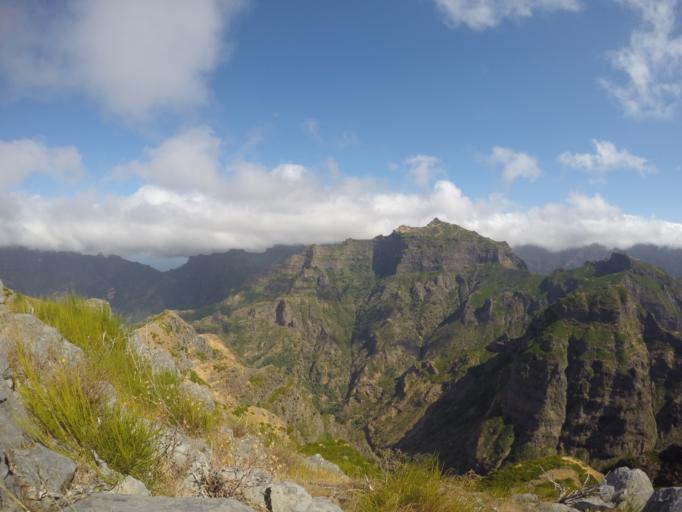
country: PT
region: Madeira
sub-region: Camara de Lobos
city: Curral das Freiras
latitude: 32.7175
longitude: -17.0000
